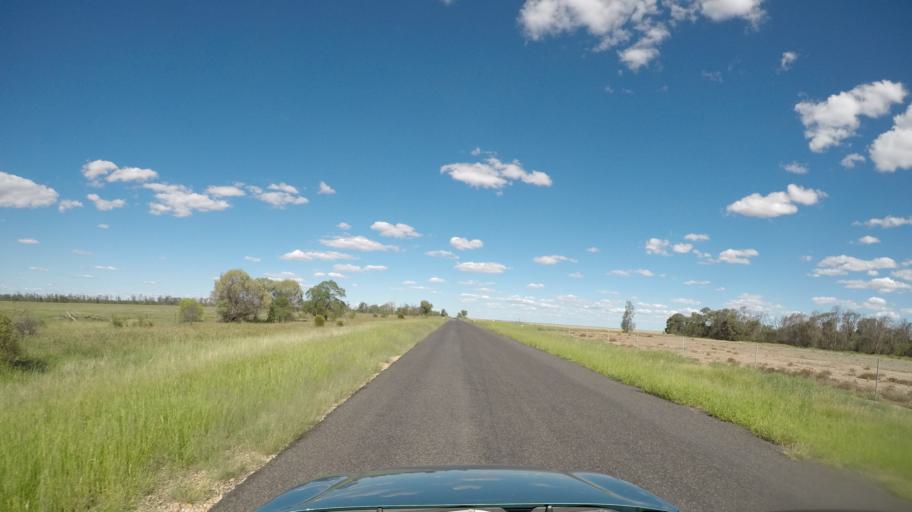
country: AU
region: Queensland
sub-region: Goondiwindi
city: Goondiwindi
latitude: -28.1609
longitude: 150.1364
